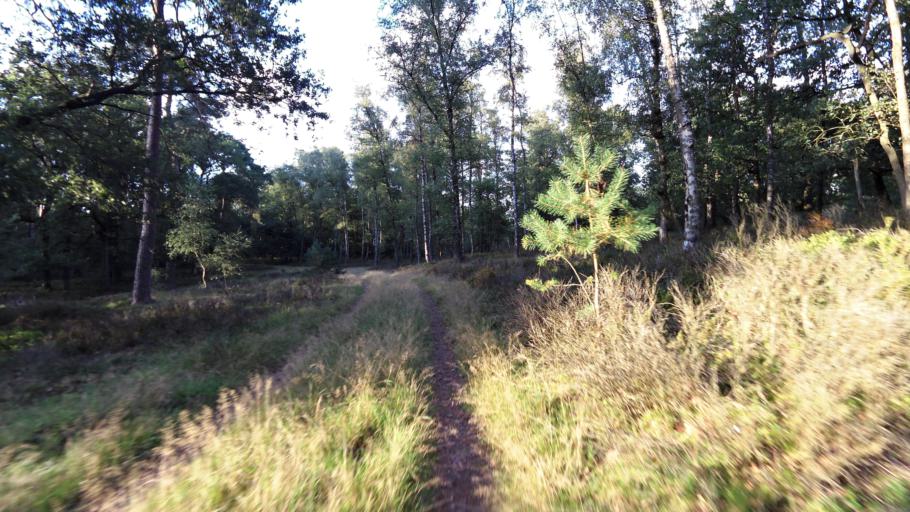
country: NL
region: Gelderland
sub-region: Gemeente Epe
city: Vaassen
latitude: 52.2962
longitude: 5.8749
